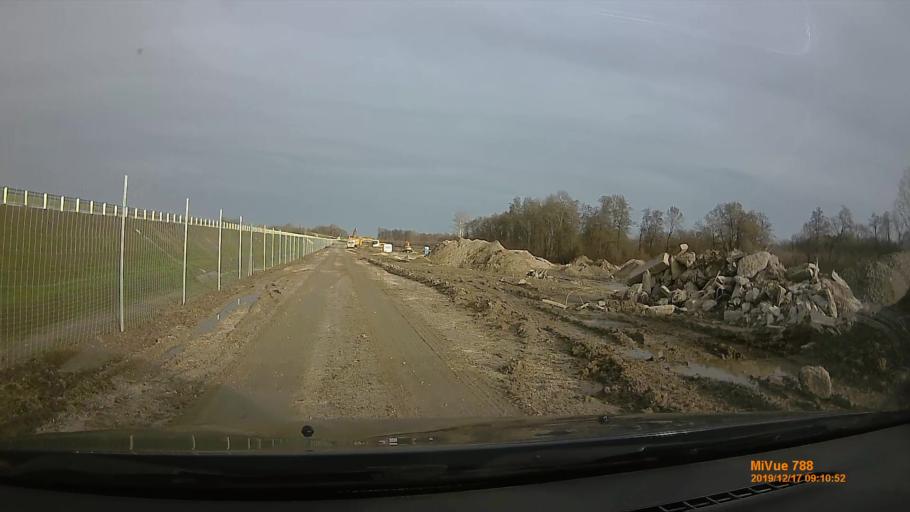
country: HU
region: Somogy
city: Karad
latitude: 46.5651
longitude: 17.8085
